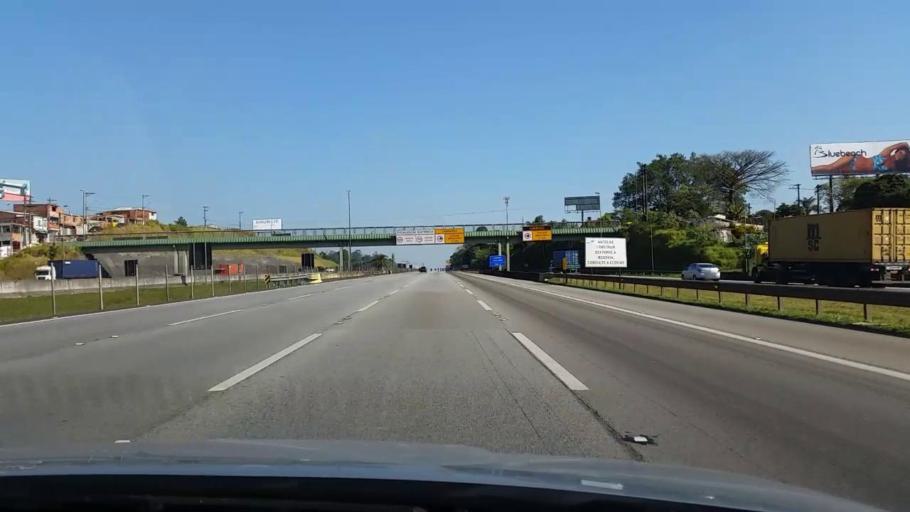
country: BR
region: Sao Paulo
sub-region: Sao Bernardo Do Campo
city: Sao Bernardo do Campo
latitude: -23.7700
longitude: -46.5927
